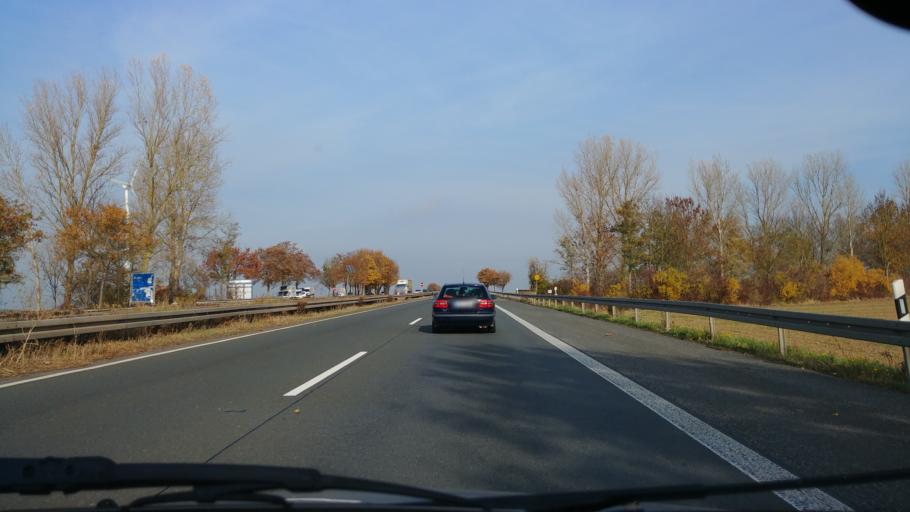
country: DE
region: Hesse
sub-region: Regierungsbezirk Giessen
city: Dehrn
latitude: 50.4169
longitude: 8.0813
